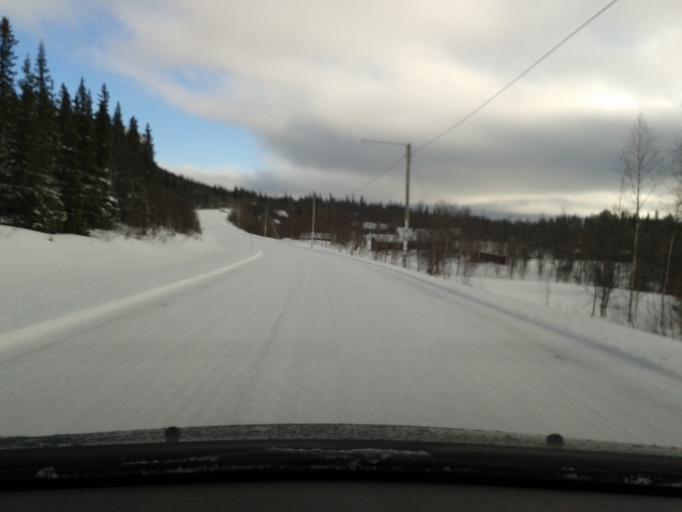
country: SE
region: Vaesterbotten
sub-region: Vilhelmina Kommun
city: Sjoberg
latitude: 65.2519
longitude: 15.5472
